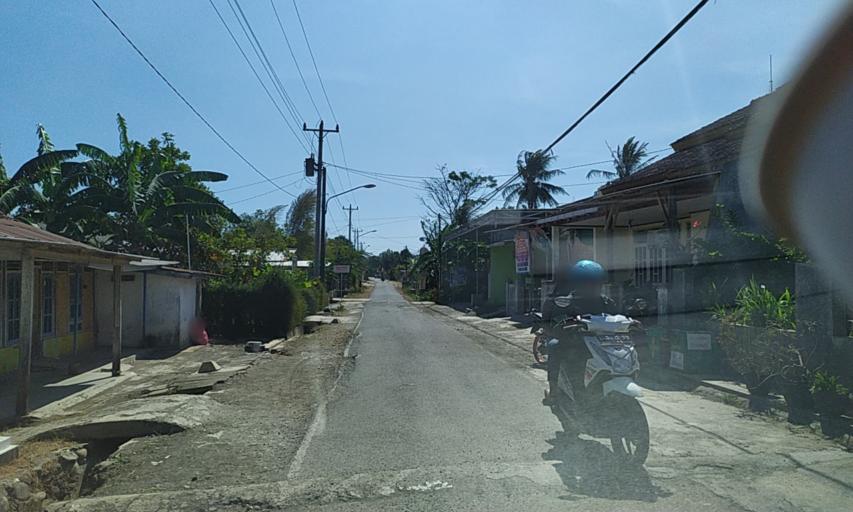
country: ID
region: Central Java
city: Kroya
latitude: -7.6289
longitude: 109.2458
